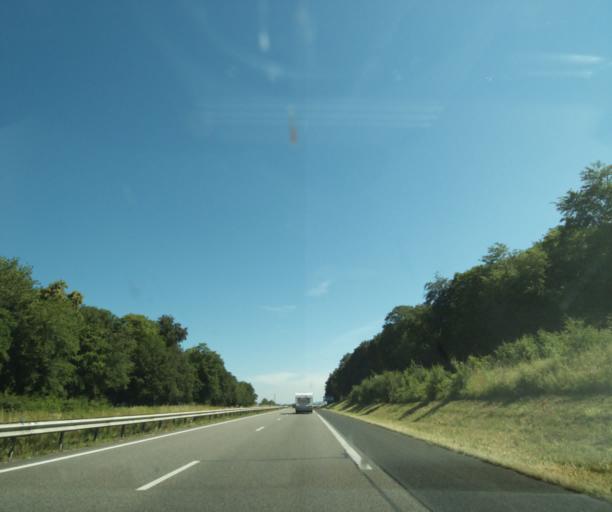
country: FR
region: Lorraine
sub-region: Departement des Vosges
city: Bulgneville
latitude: 48.2482
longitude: 5.8633
